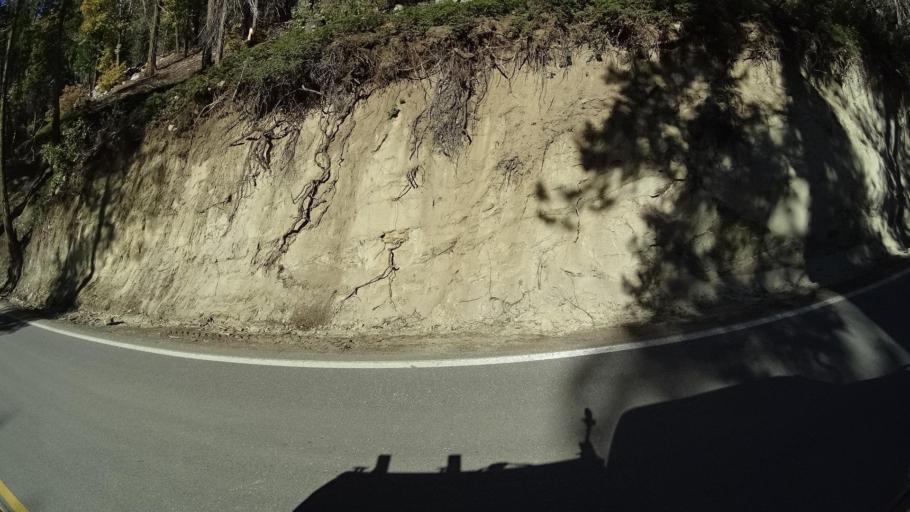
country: US
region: California
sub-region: Kern County
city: Alta Sierra
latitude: 35.7507
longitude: -118.5590
